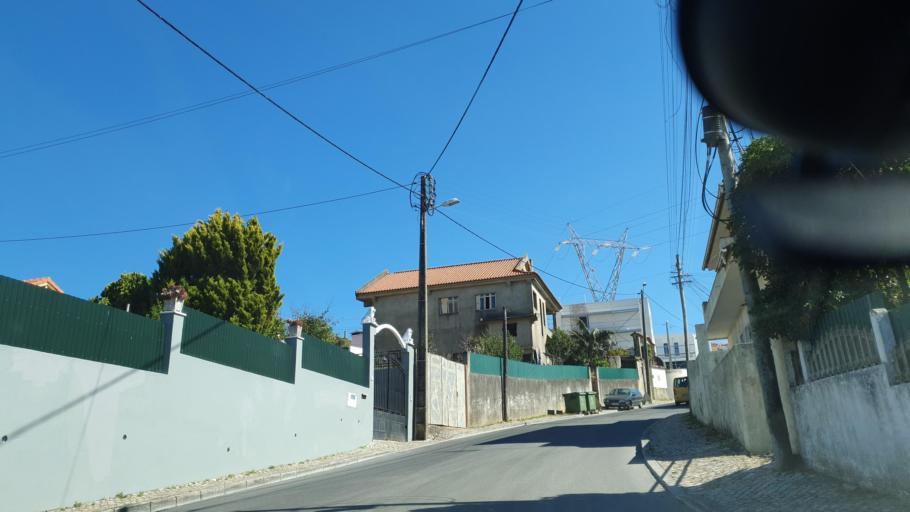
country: PT
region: Lisbon
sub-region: Sintra
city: Belas
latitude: 38.8013
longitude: -9.2510
